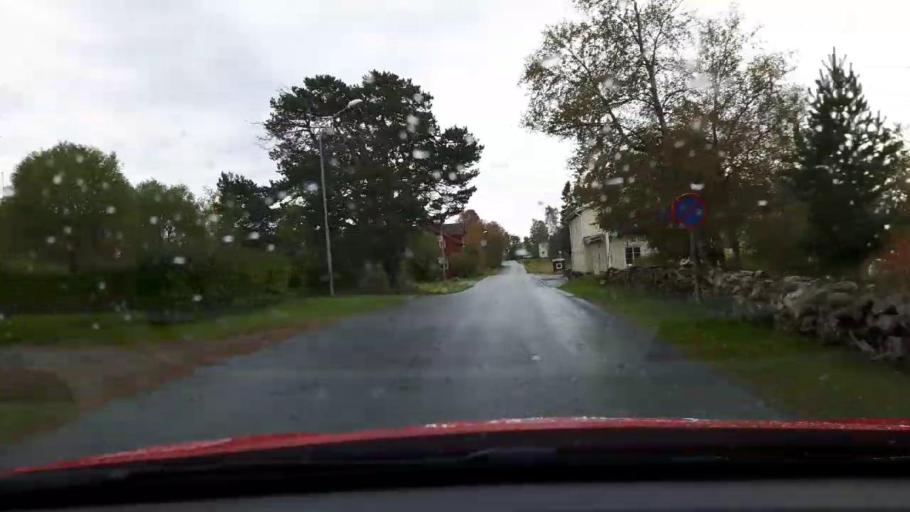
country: SE
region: Jaemtland
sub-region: Bergs Kommun
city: Hoverberg
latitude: 62.9264
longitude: 14.5160
